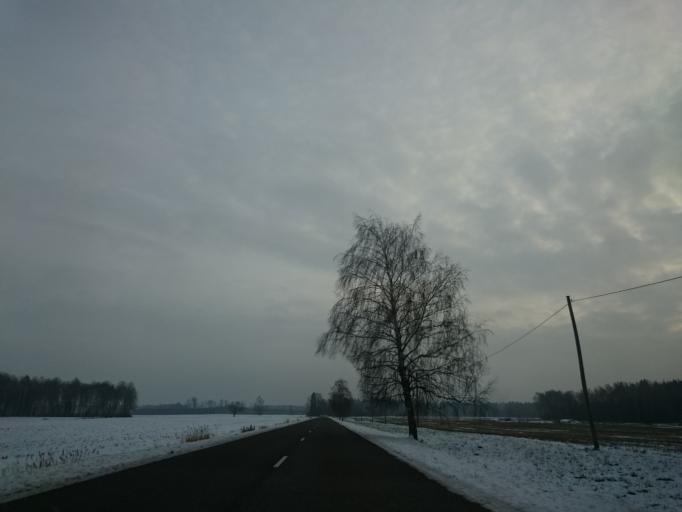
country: LV
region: Saulkrastu
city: Saulkrasti
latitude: 57.2503
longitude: 24.5091
